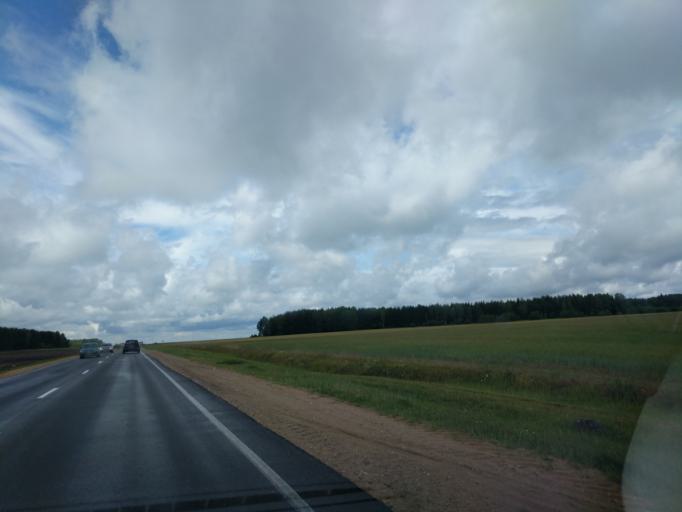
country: BY
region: Minsk
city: Il'ya
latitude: 54.3785
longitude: 27.3770
